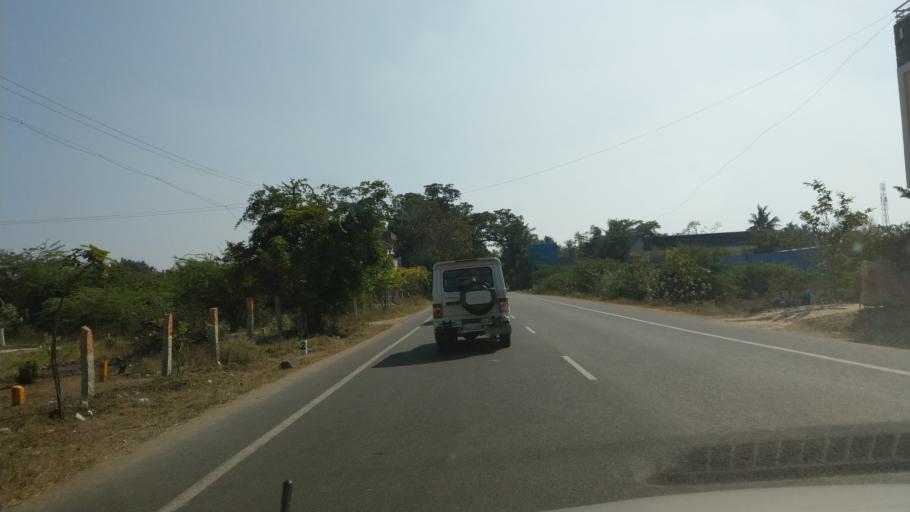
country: IN
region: Tamil Nadu
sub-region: Vellore
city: Arcot
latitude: 12.8772
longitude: 79.3153
